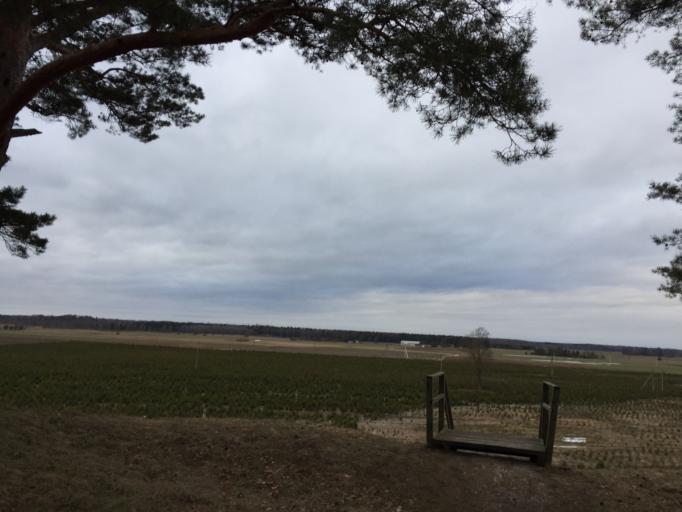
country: LT
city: Zagare
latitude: 56.3572
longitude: 23.2309
